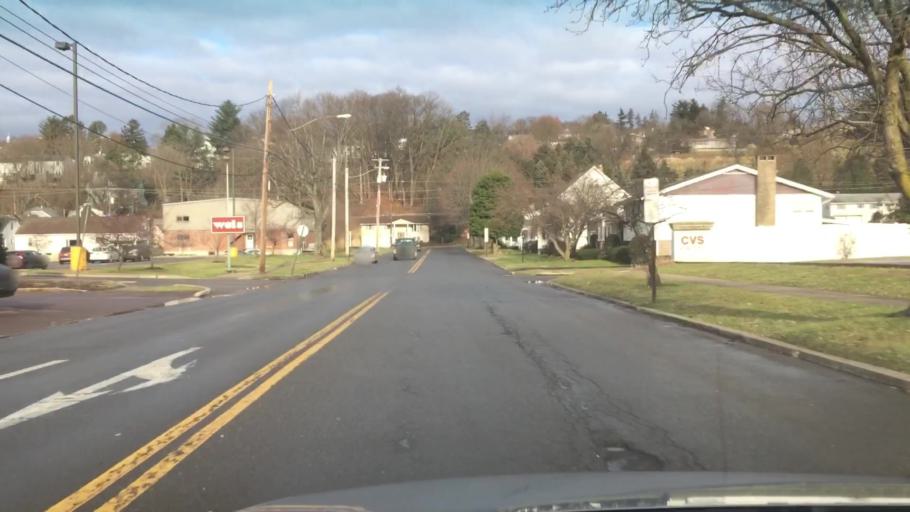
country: US
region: Pennsylvania
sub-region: Columbia County
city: Bloomsburg
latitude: 41.0035
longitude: -76.4419
